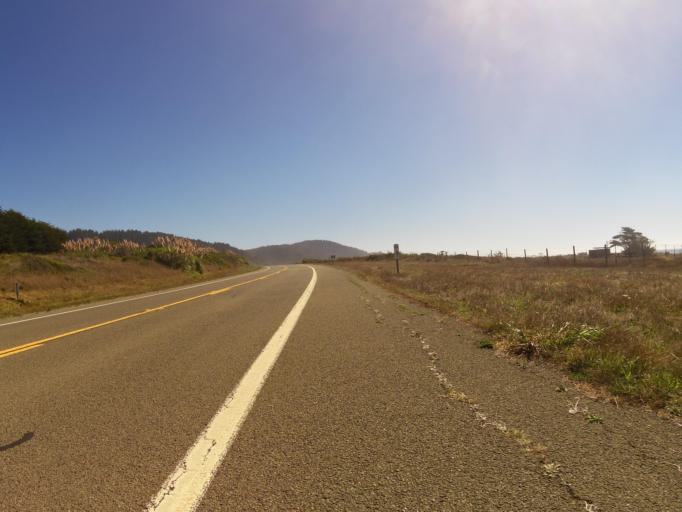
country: US
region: California
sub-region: Mendocino County
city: Fort Bragg
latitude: 39.6696
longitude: -123.7905
